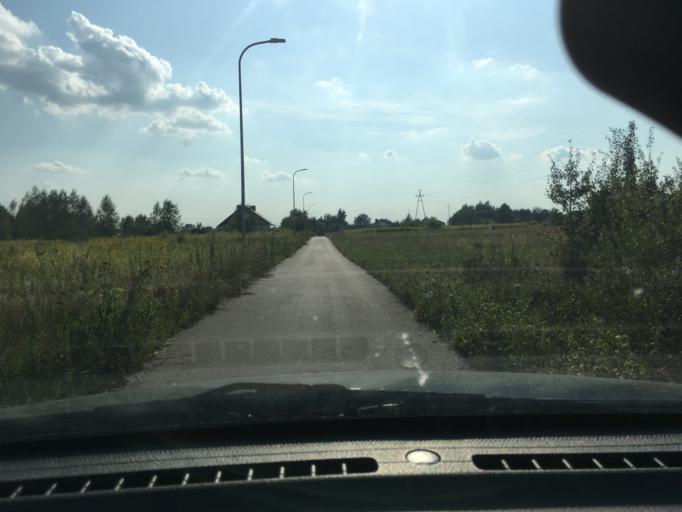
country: PL
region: Masovian Voivodeship
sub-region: Powiat piaseczynski
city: Lesznowola
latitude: 52.0533
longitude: 20.9360
